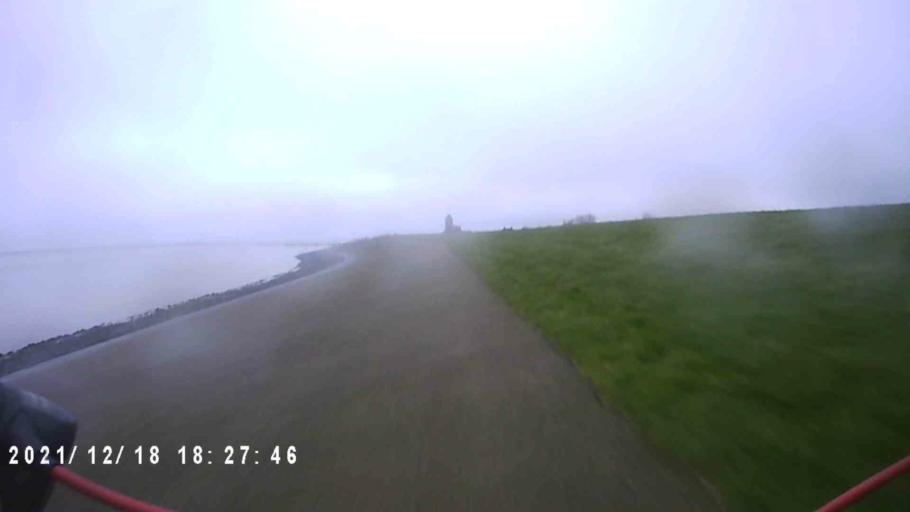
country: NL
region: Friesland
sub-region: Gemeente Dongeradeel
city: Ternaard
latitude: 53.4014
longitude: 6.0097
